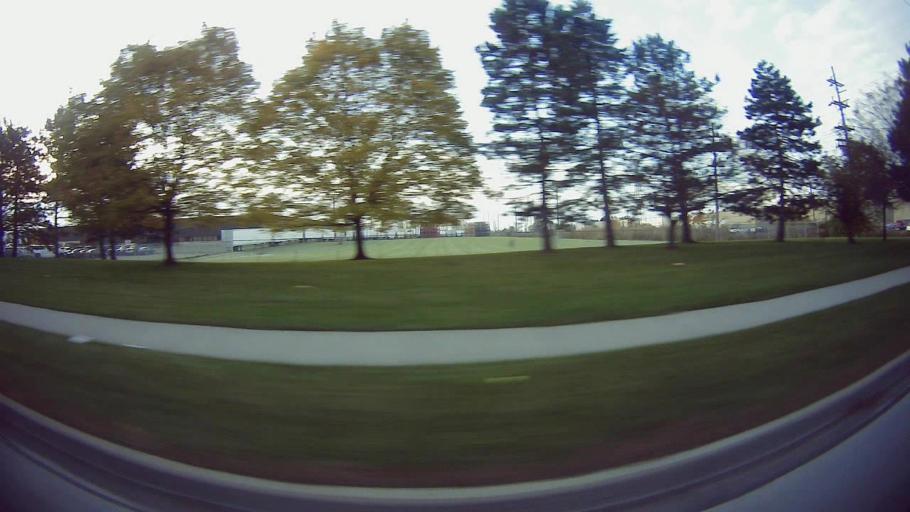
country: US
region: Michigan
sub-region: Macomb County
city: Sterling Heights
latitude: 42.5651
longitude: -83.0386
